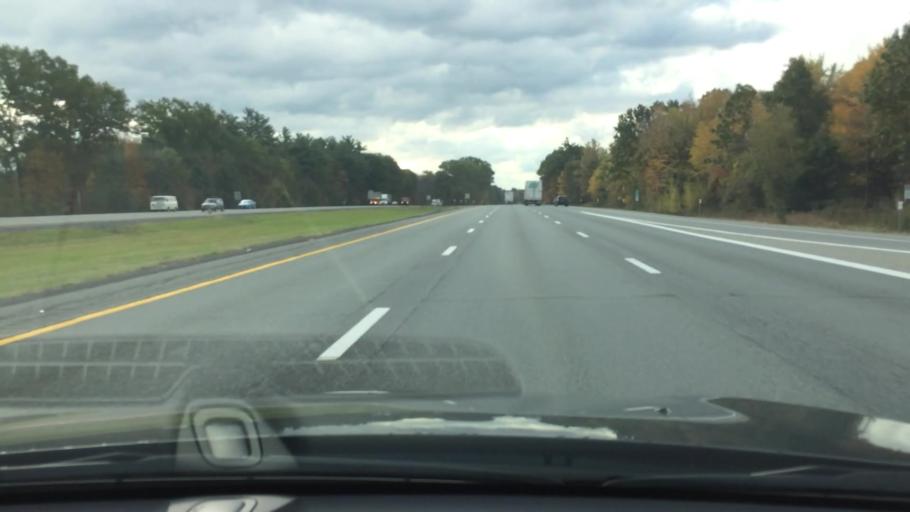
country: US
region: New York
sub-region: Saratoga County
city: Country Knolls
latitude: 42.9683
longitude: -73.8020
